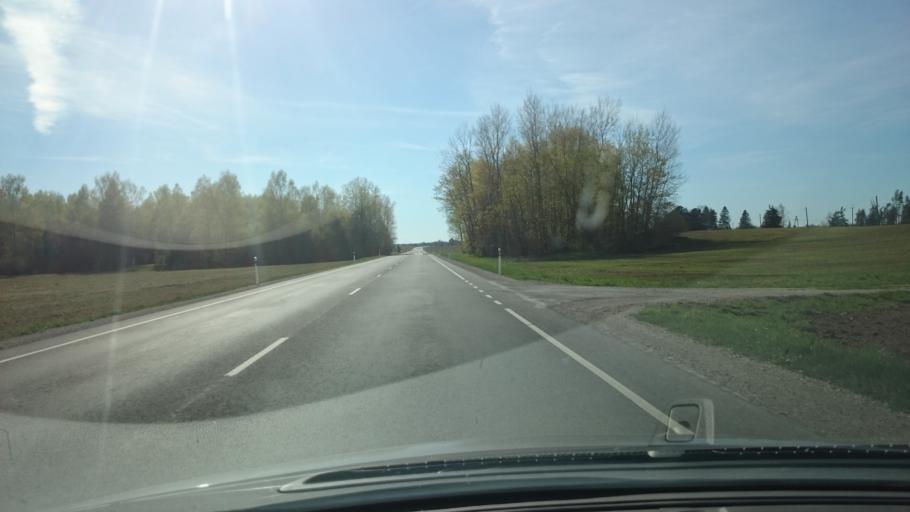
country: EE
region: Laeaene-Virumaa
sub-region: Haljala vald
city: Haljala
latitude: 59.3486
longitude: 26.2694
